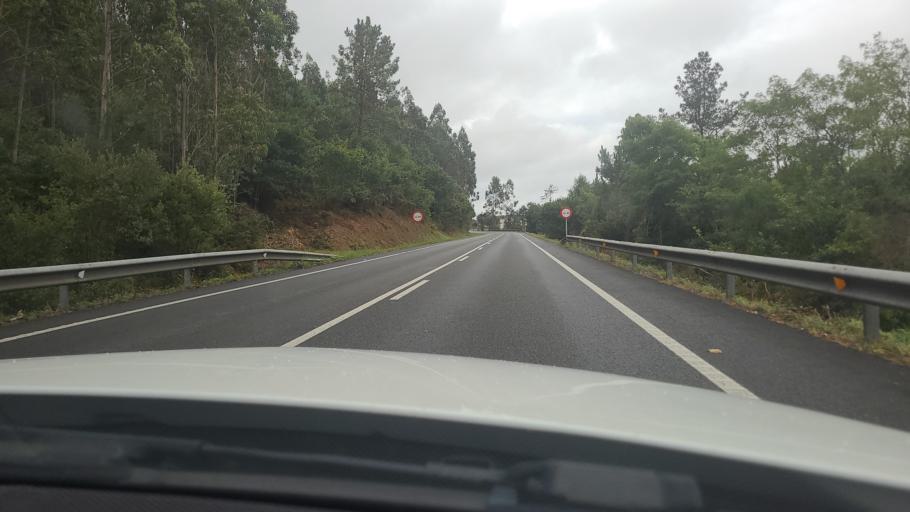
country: ES
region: Galicia
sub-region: Provincia da Coruna
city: Cee
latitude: 42.9999
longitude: -9.1775
